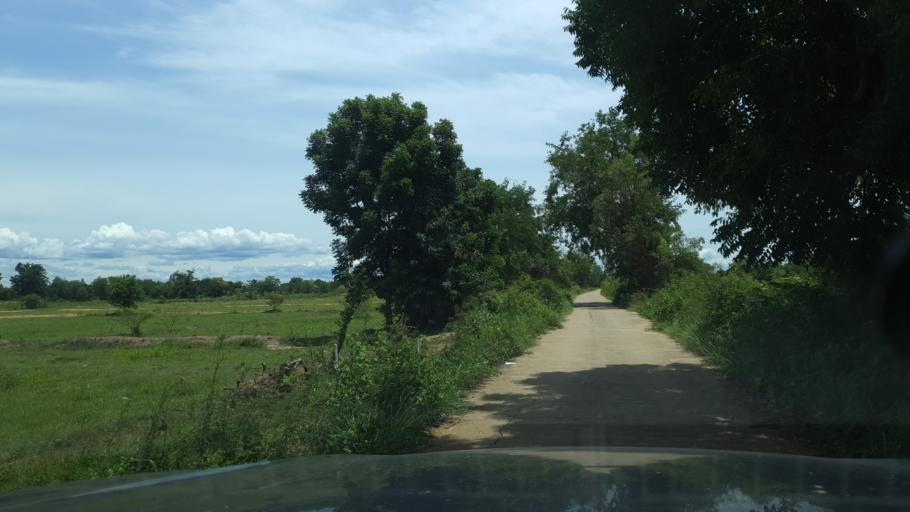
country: TH
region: Sukhothai
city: Ban Na
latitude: 17.0881
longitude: 99.6871
